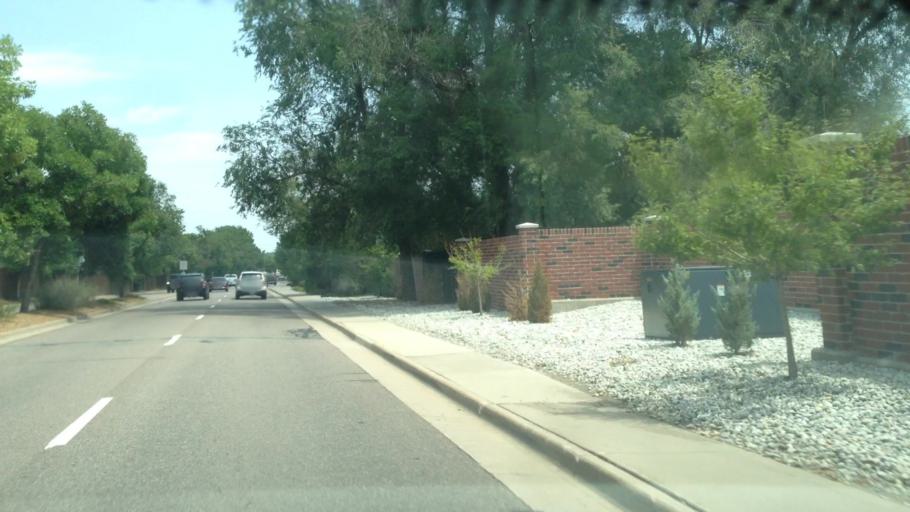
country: US
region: Colorado
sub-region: Arapahoe County
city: Columbine Valley
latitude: 39.6101
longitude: -105.0338
